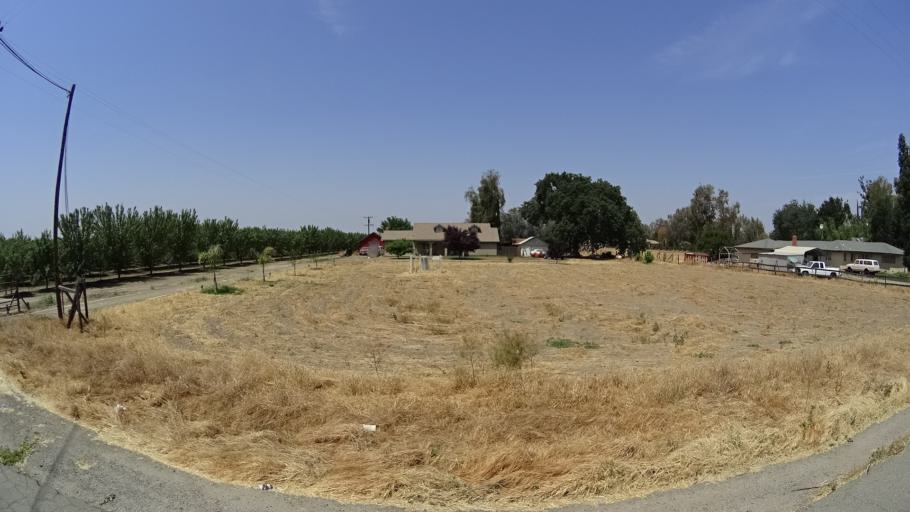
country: US
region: California
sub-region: Kings County
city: Lemoore
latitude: 36.3392
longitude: -119.7808
